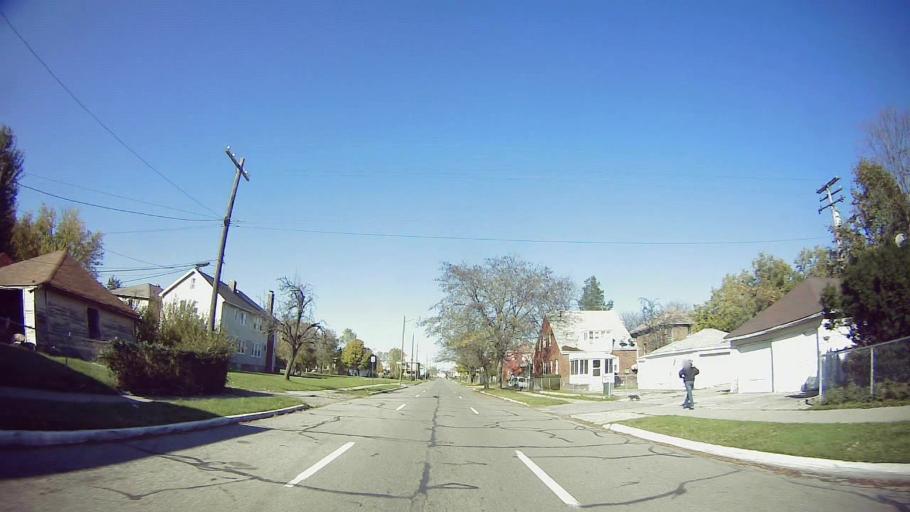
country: US
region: Michigan
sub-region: Wayne County
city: Highland Park
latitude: 42.3963
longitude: -83.1167
